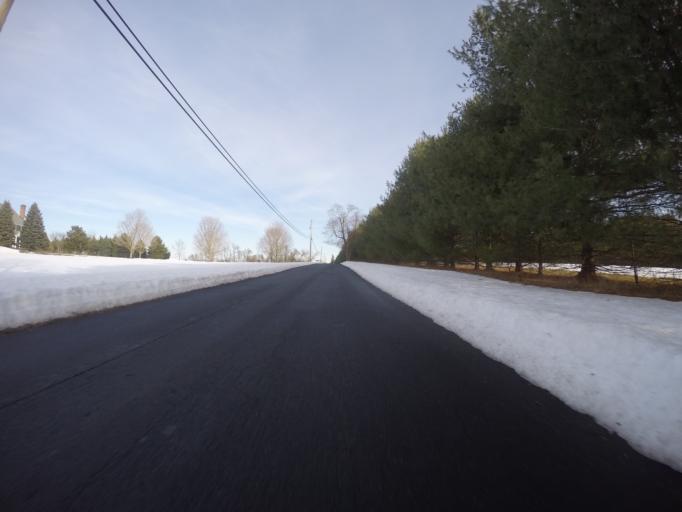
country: US
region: Maryland
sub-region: Baltimore County
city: Hunt Valley
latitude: 39.5475
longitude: -76.5727
